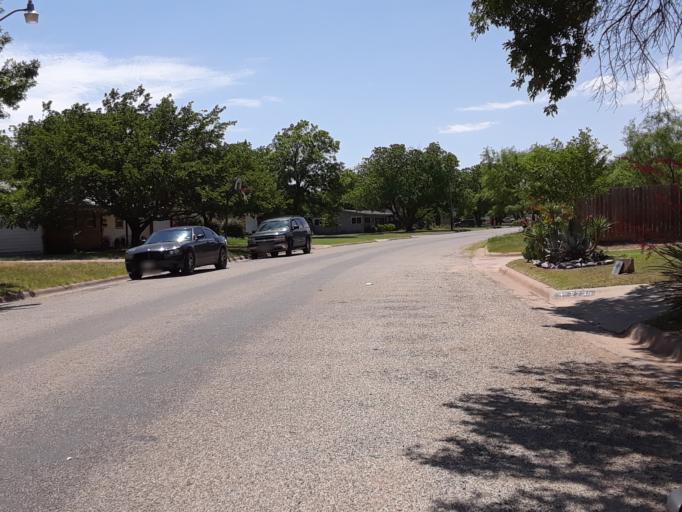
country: US
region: Texas
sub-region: Taylor County
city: Abilene
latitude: 32.4108
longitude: -99.7500
